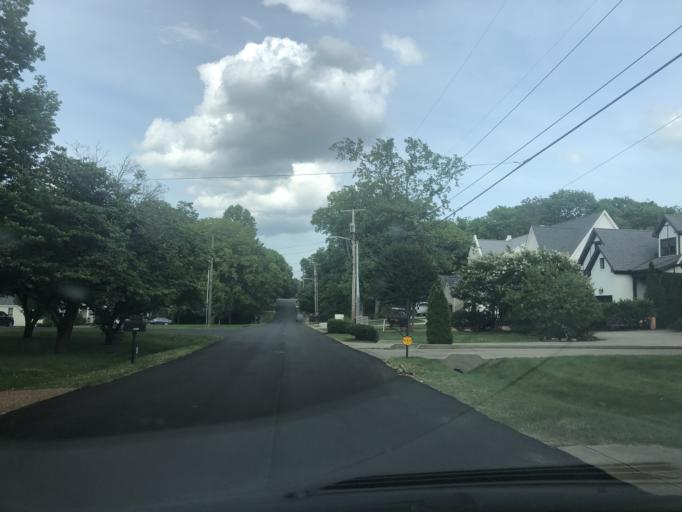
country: US
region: Tennessee
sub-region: Davidson County
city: Oak Hill
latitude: 36.0979
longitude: -86.7892
